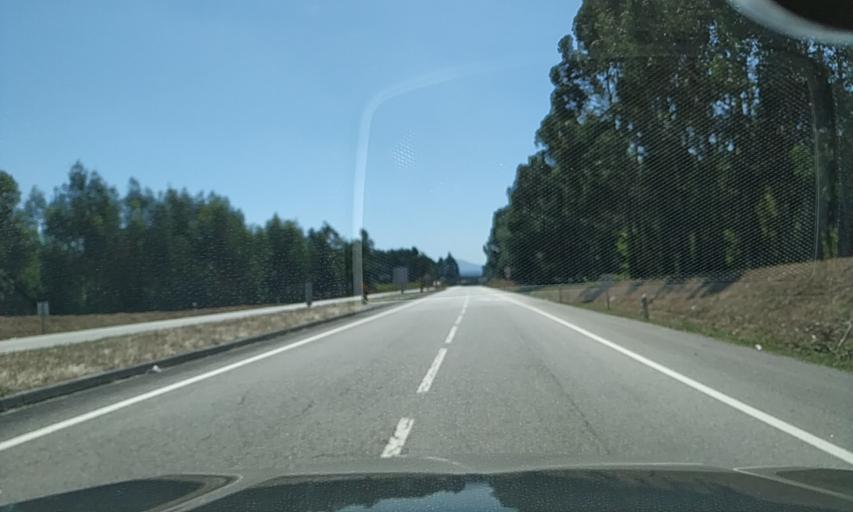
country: PT
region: Aveiro
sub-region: Agueda
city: Agueda
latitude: 40.5496
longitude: -8.4714
